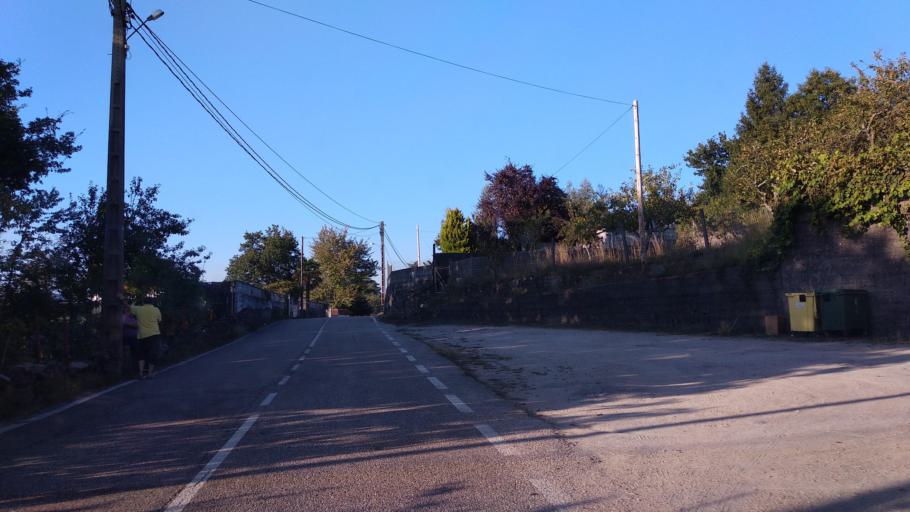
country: ES
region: Galicia
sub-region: Provincia de Pontevedra
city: Ponte Caldelas
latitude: 42.3604
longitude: -8.5313
